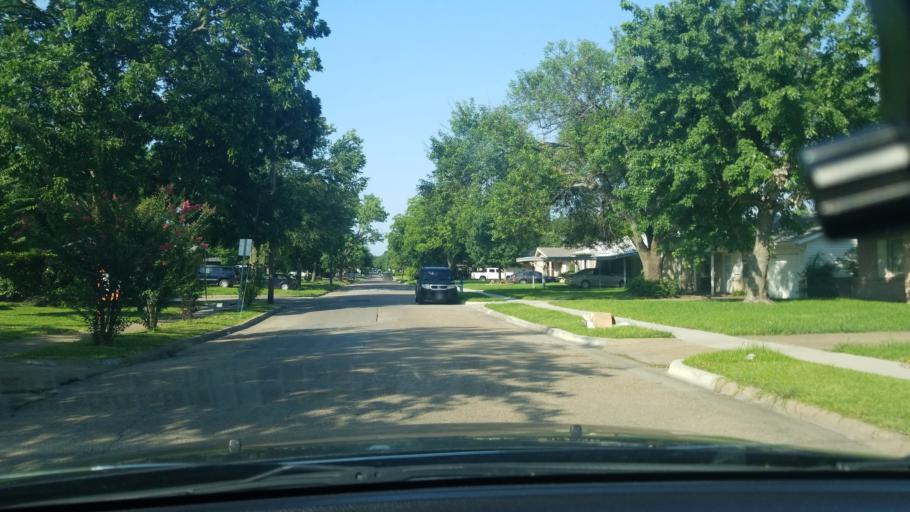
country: US
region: Texas
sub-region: Dallas County
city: Mesquite
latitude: 32.8259
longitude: -96.6352
